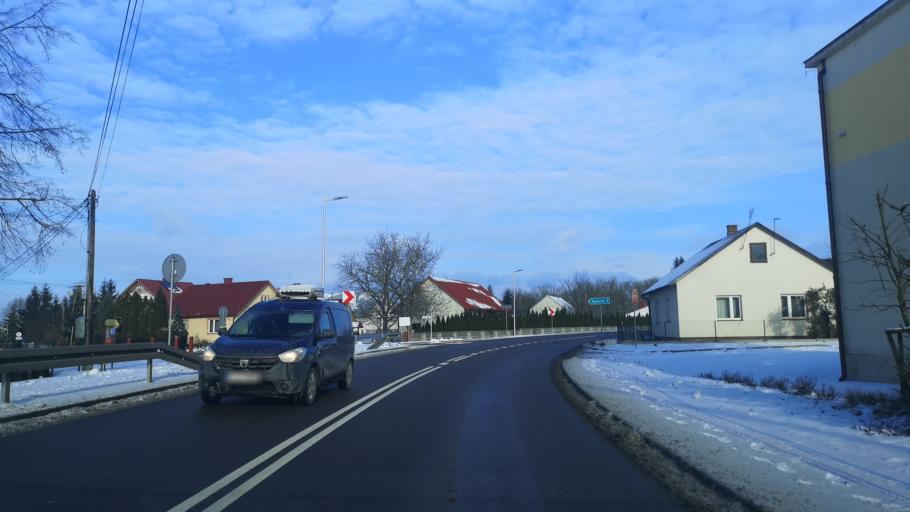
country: PL
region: Subcarpathian Voivodeship
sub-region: Powiat przeworski
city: Tryncza
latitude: 50.1648
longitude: 22.5803
